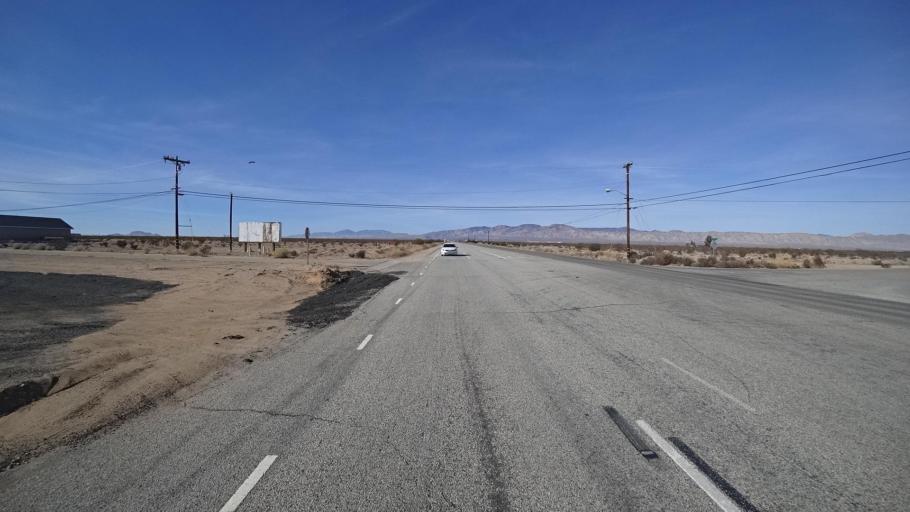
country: US
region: California
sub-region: Kern County
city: California City
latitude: 35.1256
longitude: -118.0124
